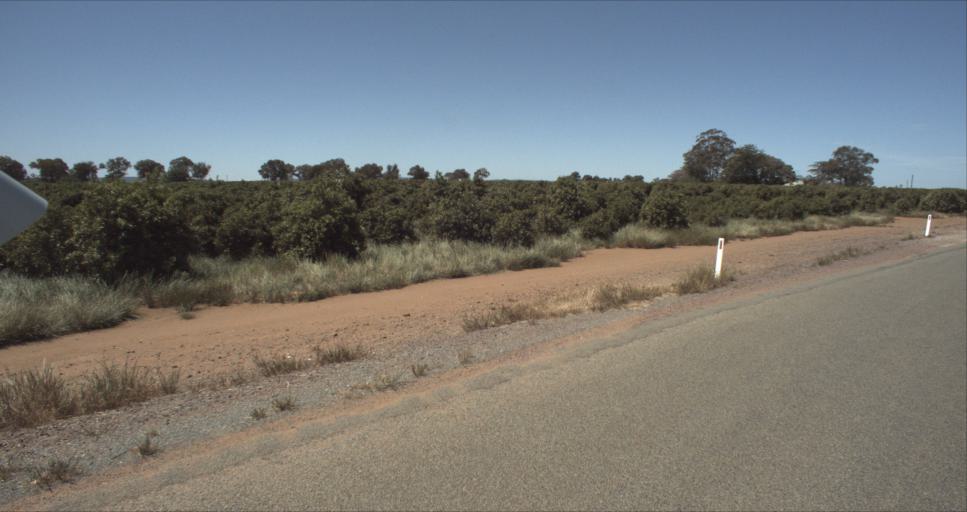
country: AU
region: New South Wales
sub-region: Leeton
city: Leeton
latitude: -34.5340
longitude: 146.3555
